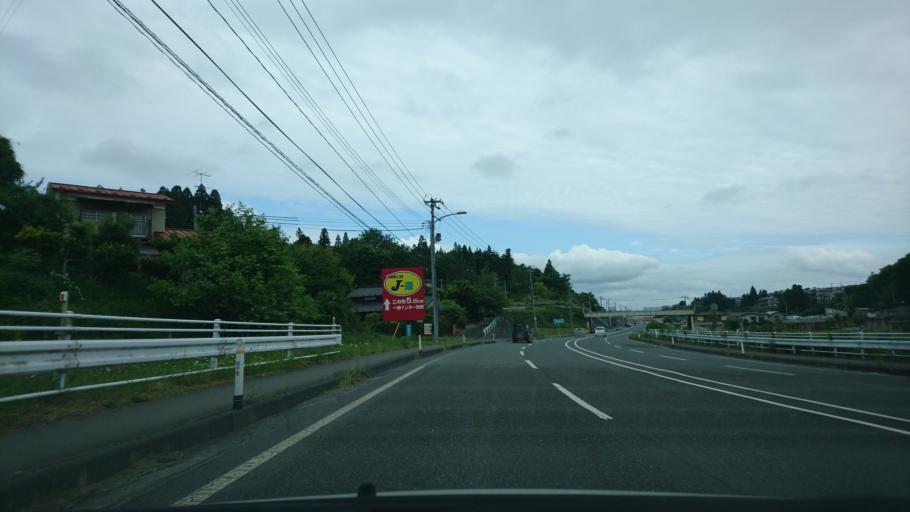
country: JP
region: Iwate
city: Ichinoseki
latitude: 38.9133
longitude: 141.1427
